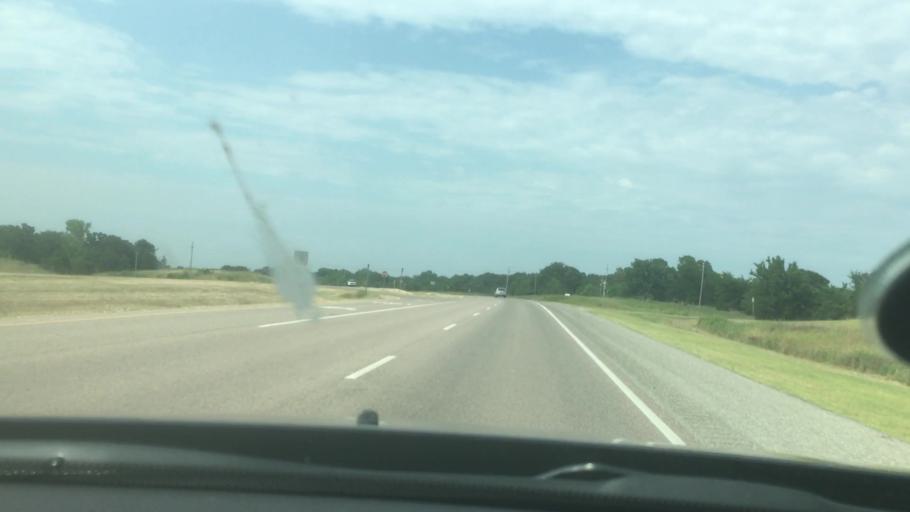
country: US
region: Oklahoma
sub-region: Pontotoc County
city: Ada
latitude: 34.8150
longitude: -96.6944
